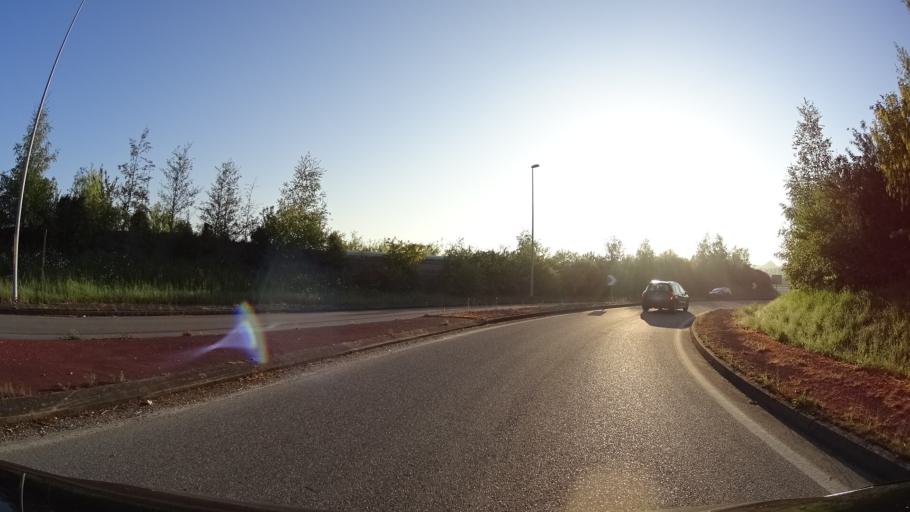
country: FR
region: Brittany
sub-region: Departement d'Ille-et-Vilaine
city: Bruz
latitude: 48.0276
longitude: -1.7682
